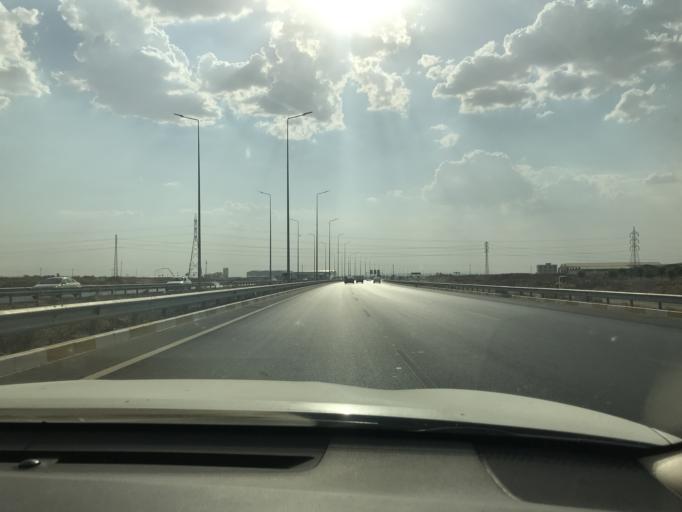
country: IQ
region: Arbil
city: Erbil
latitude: 36.1364
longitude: 43.9978
